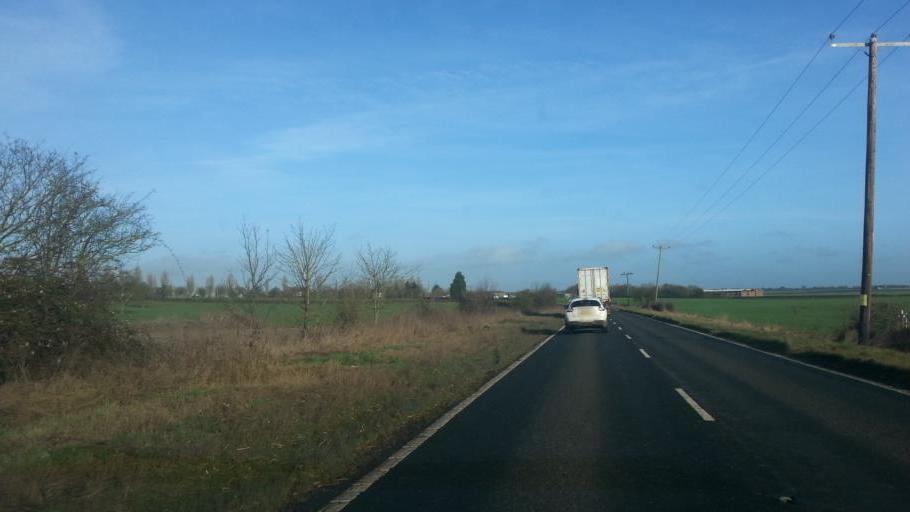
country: GB
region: England
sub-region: Cambridgeshire
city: Ramsey
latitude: 52.4251
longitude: -0.1052
